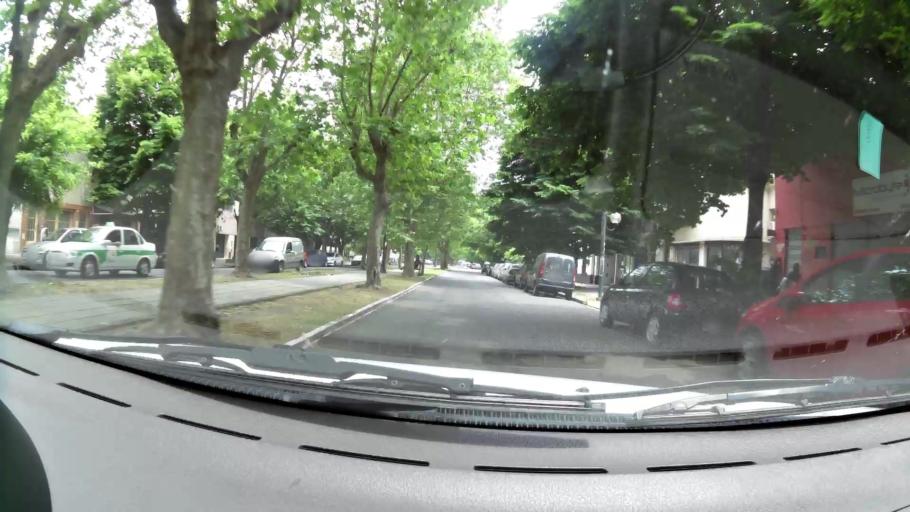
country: AR
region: Buenos Aires
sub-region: Partido de La Plata
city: La Plata
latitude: -34.9241
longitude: -57.9586
